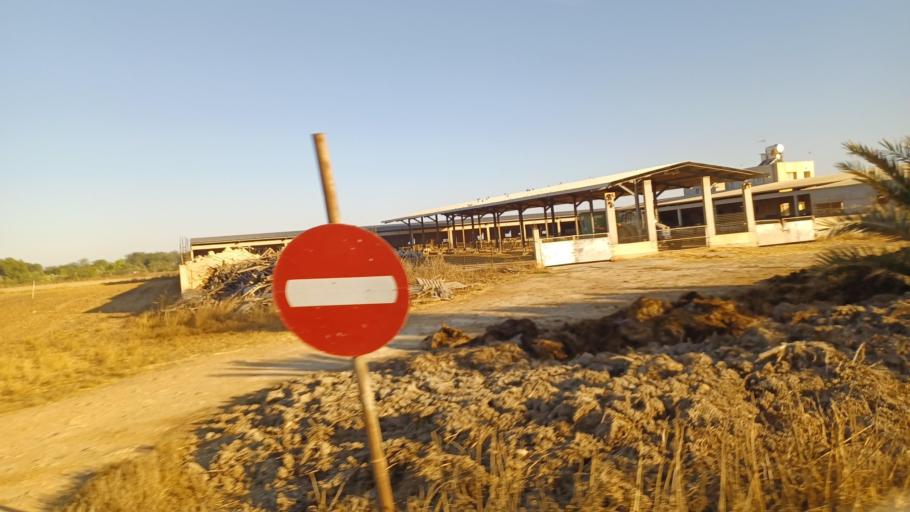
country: CY
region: Ammochostos
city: Avgorou
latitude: 35.0057
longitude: 33.8354
